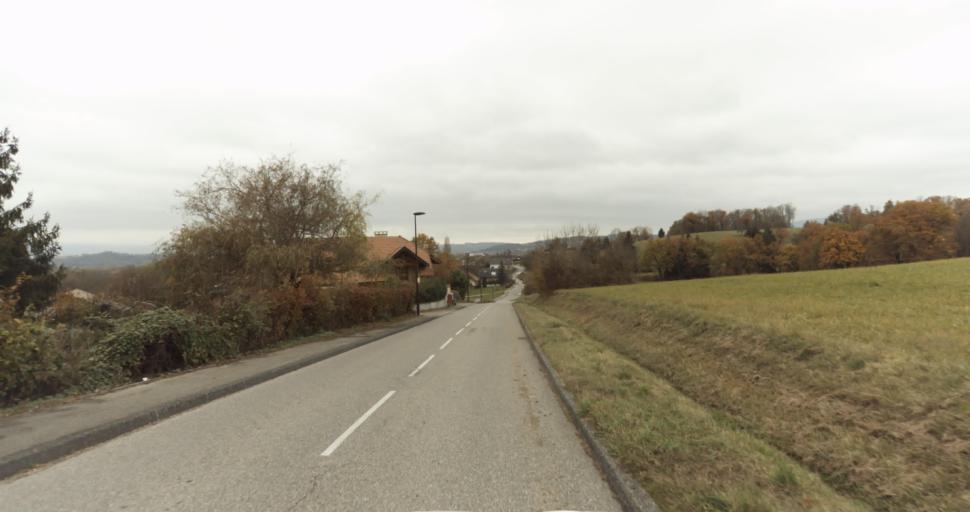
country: FR
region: Rhone-Alpes
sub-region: Departement de la Haute-Savoie
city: Chavanod
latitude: 45.8749
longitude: 6.0637
